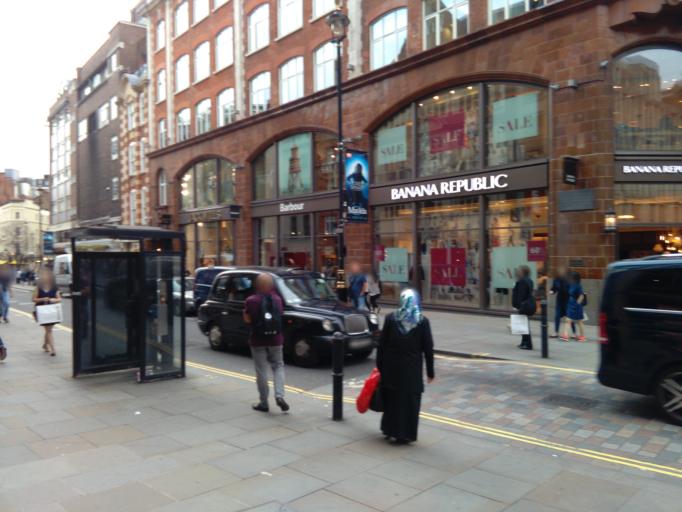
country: GB
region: England
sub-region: Greater London
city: London
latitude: 51.5124
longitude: -0.1258
